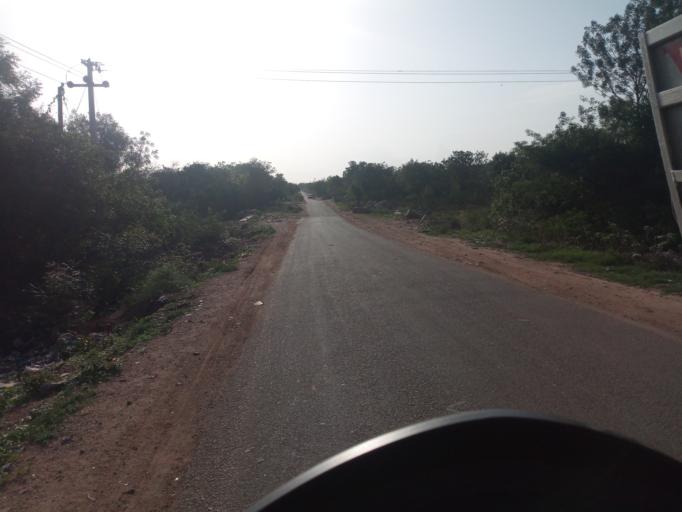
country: IN
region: Telangana
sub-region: Rangareddi
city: Quthbullapur
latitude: 17.5523
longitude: 78.4196
